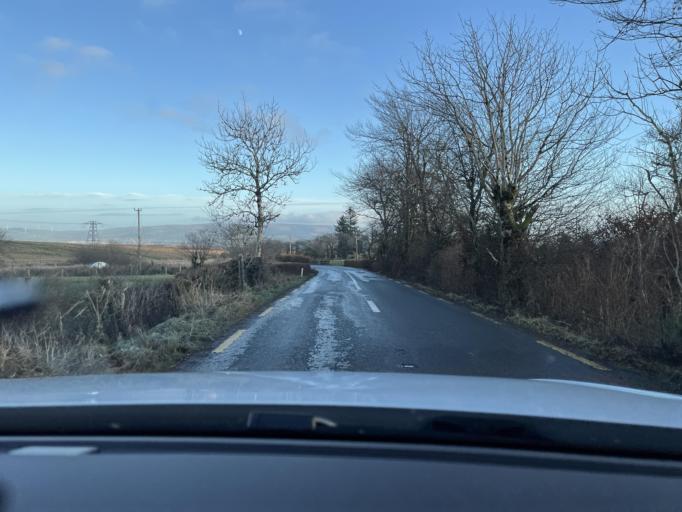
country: IE
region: Ulster
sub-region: An Cabhan
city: Ballyconnell
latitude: 54.1660
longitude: -7.7991
